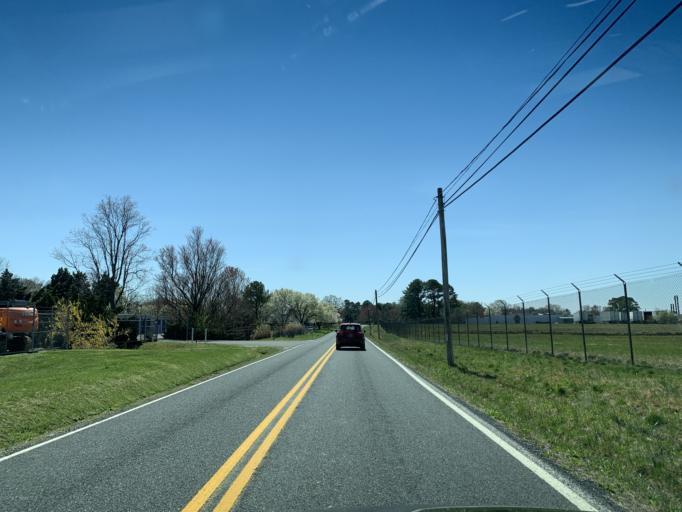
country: US
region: Maryland
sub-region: Talbot County
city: Easton
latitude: 38.7985
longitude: -76.0640
